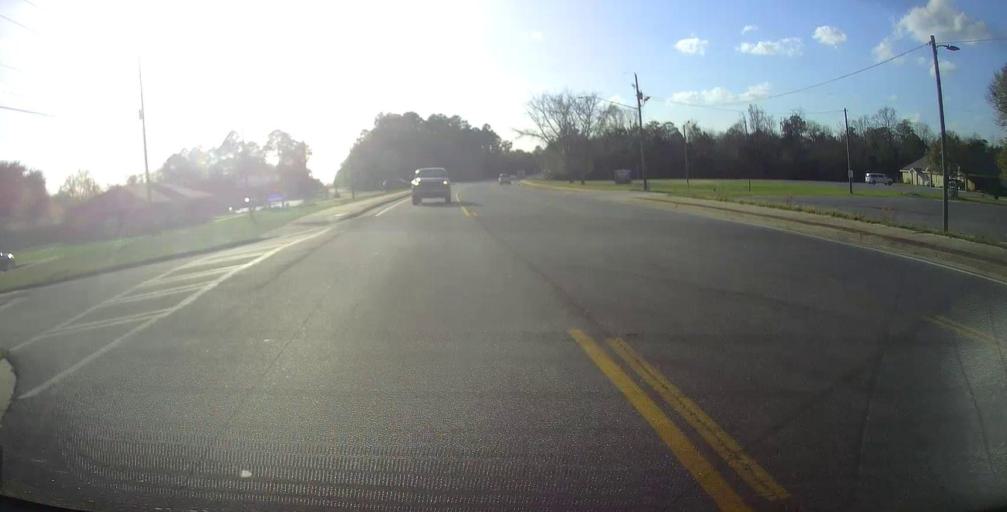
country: US
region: Georgia
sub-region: Tattnall County
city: Reidsville
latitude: 32.0806
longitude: -82.1286
